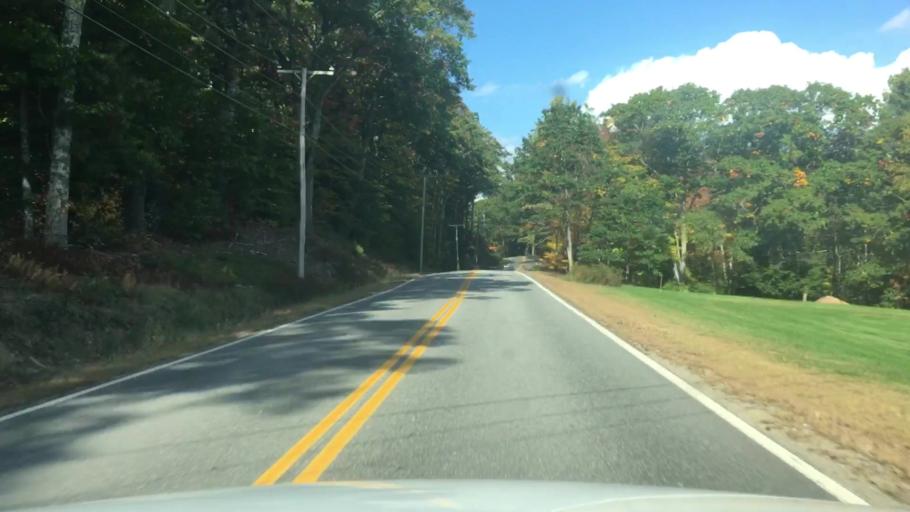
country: US
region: Maine
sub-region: Knox County
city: Union
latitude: 44.2417
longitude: -69.2784
